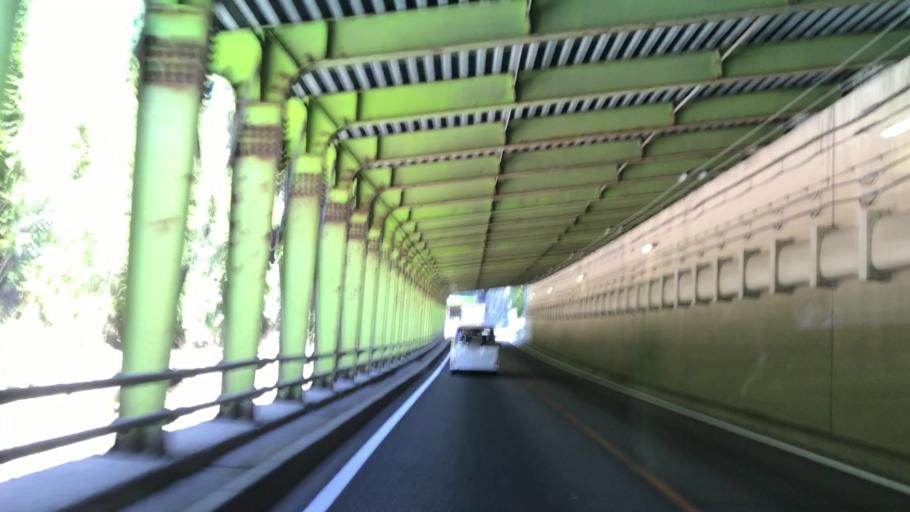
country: JP
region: Hokkaido
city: Shimo-furano
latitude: 42.9364
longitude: 142.6001
